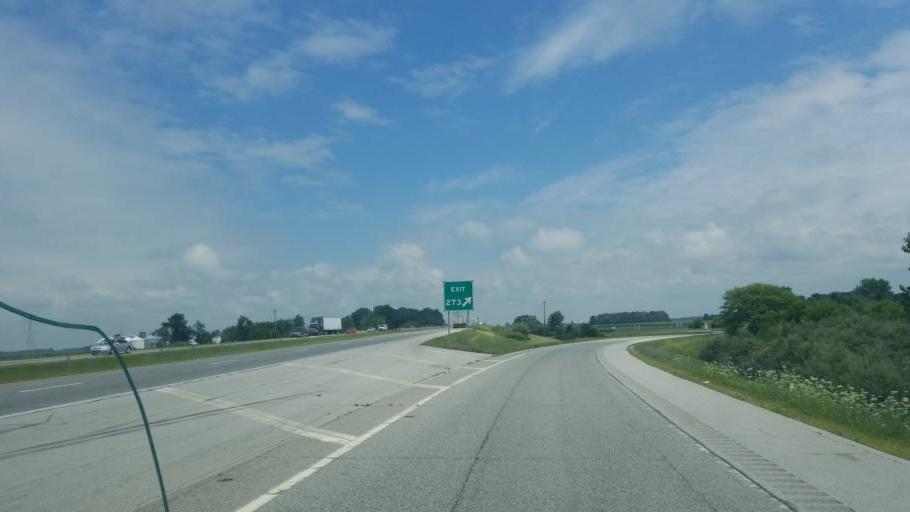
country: US
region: Indiana
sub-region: Huntington County
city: Warren
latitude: 40.6659
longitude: -85.4950
